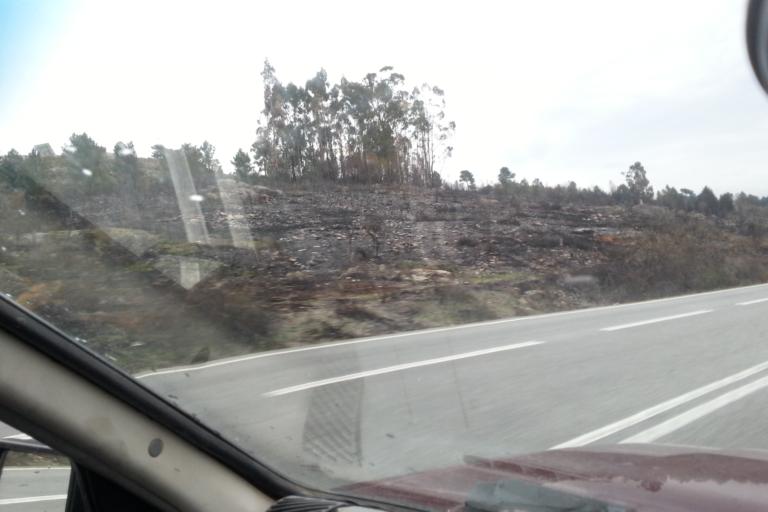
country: PT
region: Guarda
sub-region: Fornos de Algodres
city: Fornos de Algodres
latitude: 40.6025
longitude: -7.5510
